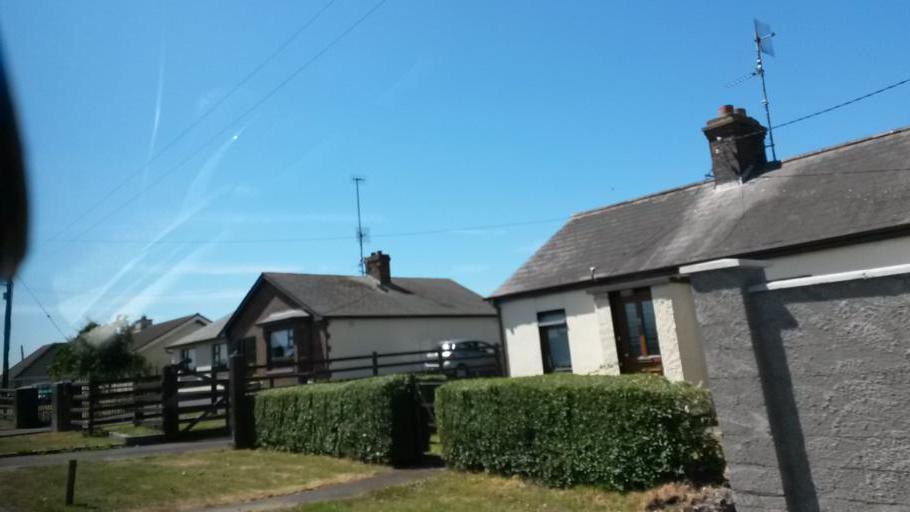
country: IE
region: Leinster
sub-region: Fingal County
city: Swords
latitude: 53.4988
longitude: -6.2701
